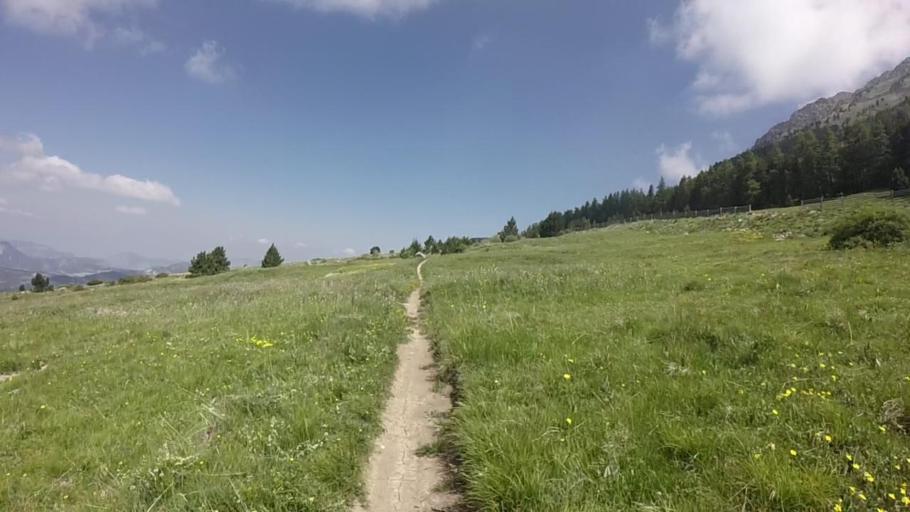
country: FR
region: Provence-Alpes-Cote d'Azur
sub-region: Departement des Alpes-de-Haute-Provence
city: Seyne-les-Alpes
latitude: 44.4001
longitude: 6.3765
